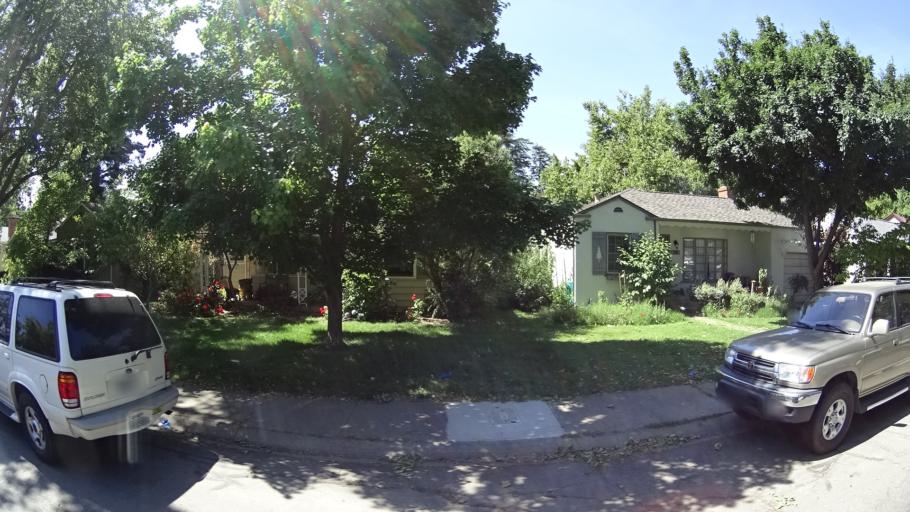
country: US
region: California
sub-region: Sacramento County
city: Sacramento
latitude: 38.5532
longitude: -121.5080
